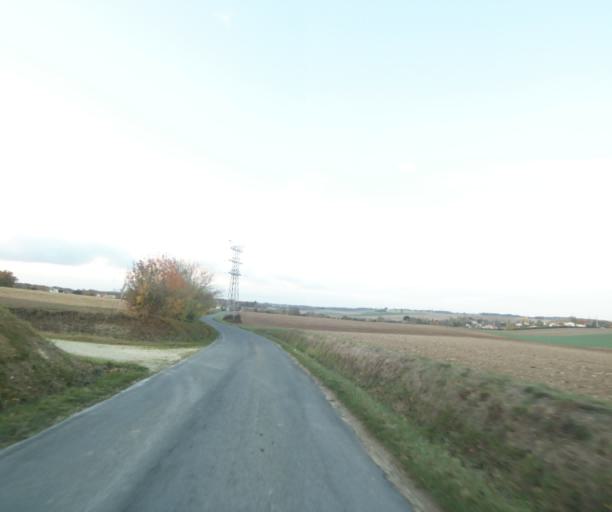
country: FR
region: Poitou-Charentes
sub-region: Departement de la Charente-Maritime
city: Saintes
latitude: 45.7627
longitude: -0.6508
